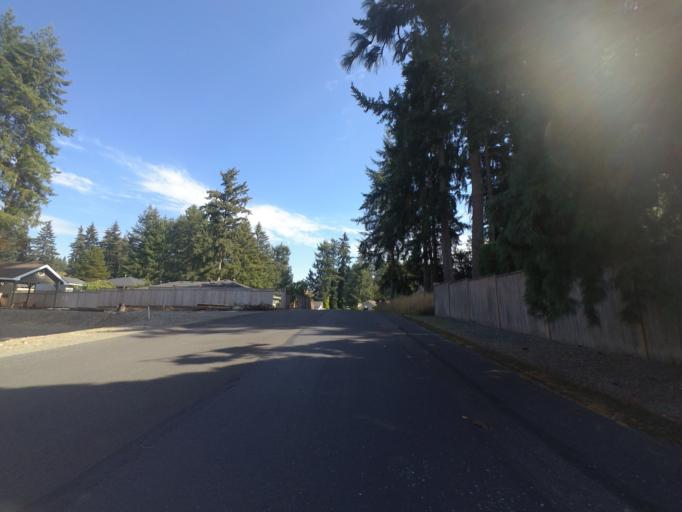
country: US
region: Washington
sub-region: Pierce County
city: University Place
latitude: 47.2149
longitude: -122.5335
